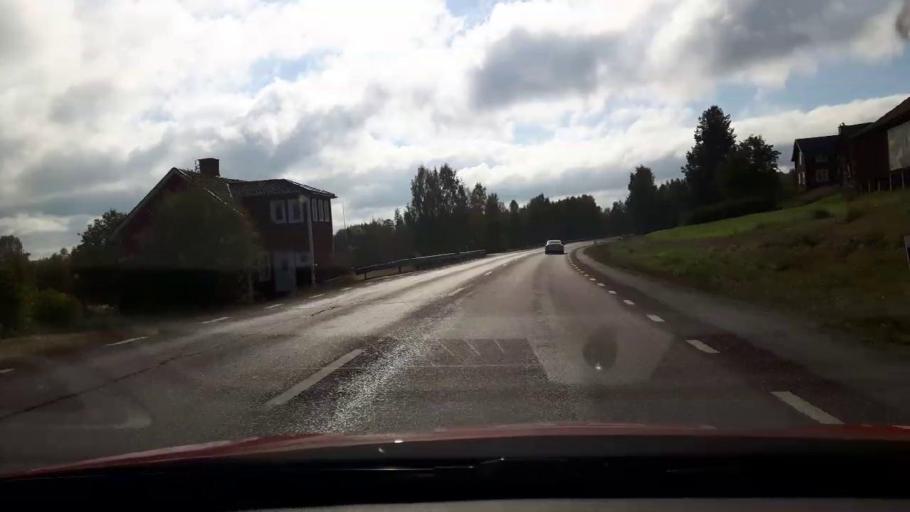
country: SE
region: Gaevleborg
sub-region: Ljusdals Kommun
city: Jaervsoe
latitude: 61.7264
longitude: 16.1683
